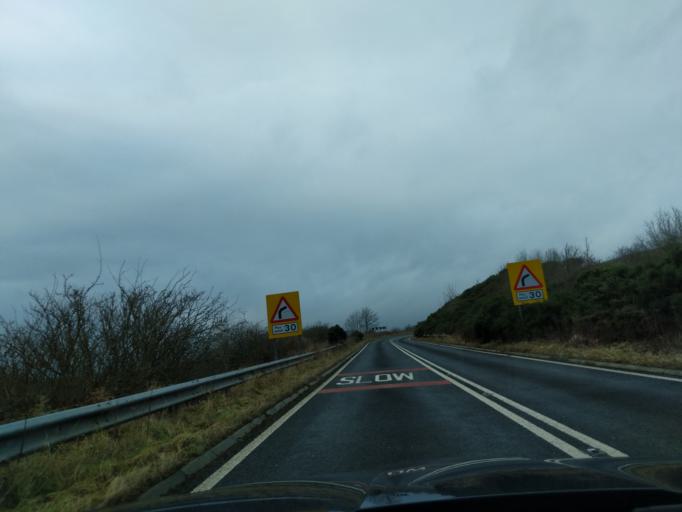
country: GB
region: England
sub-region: Northumberland
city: Rothley
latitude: 55.1593
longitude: -2.0139
